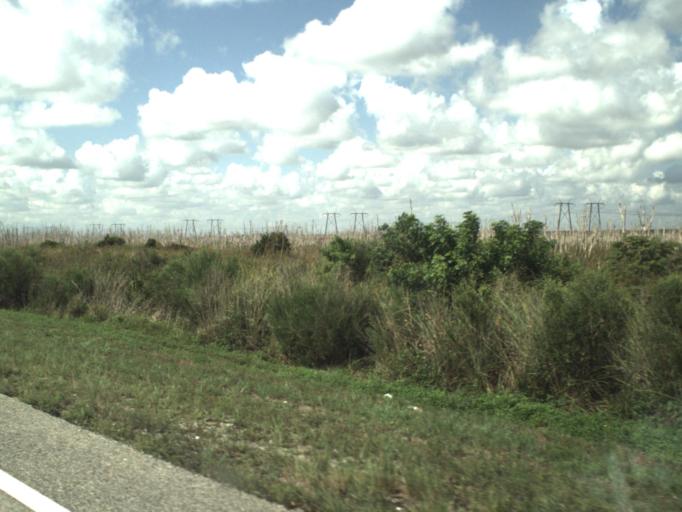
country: US
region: Florida
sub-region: Broward County
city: Weston
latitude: 25.9978
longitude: -80.4326
